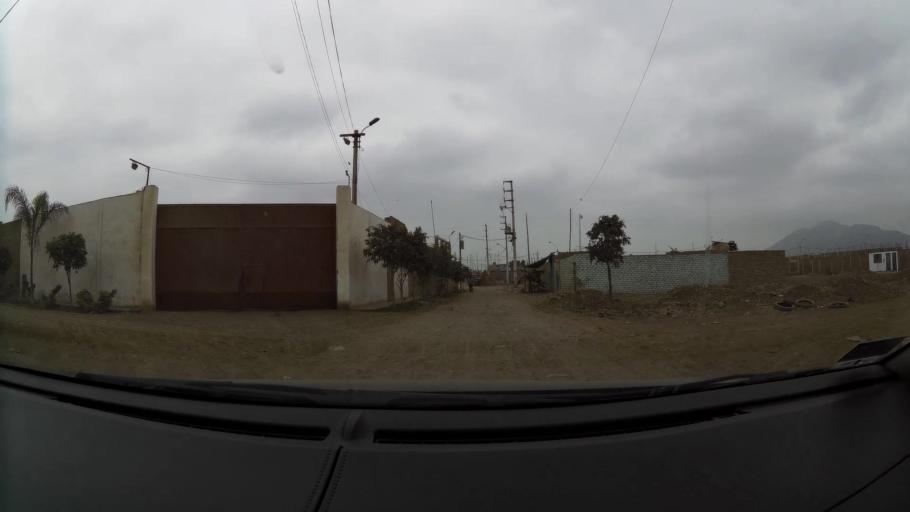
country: PE
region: Lima
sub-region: Provincia de Huaral
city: Huaral
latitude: -11.4994
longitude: -77.1992
